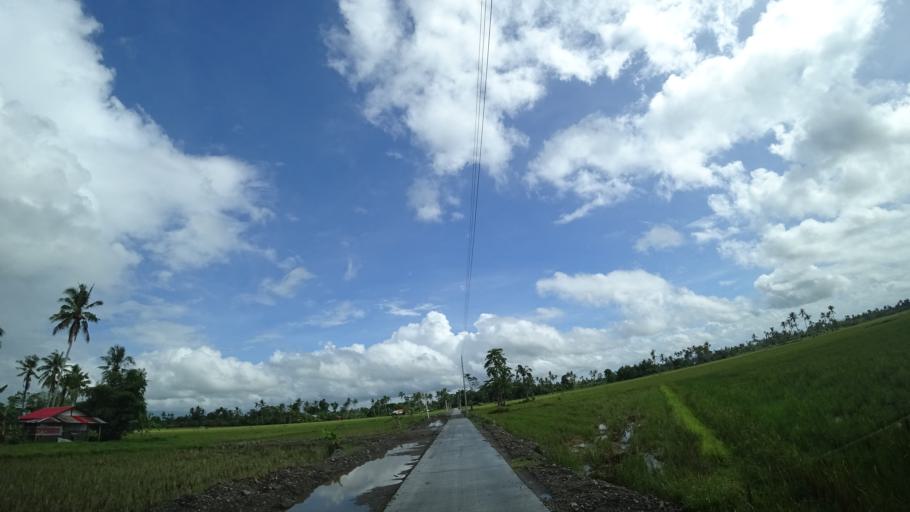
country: PH
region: Eastern Visayas
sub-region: Province of Leyte
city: Cabacungan
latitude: 10.9114
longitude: 124.9774
